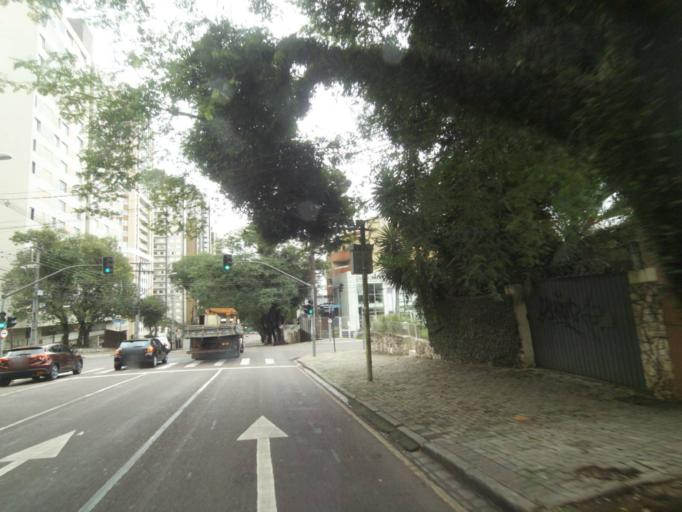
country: BR
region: Parana
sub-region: Curitiba
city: Curitiba
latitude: -25.4301
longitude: -49.2958
